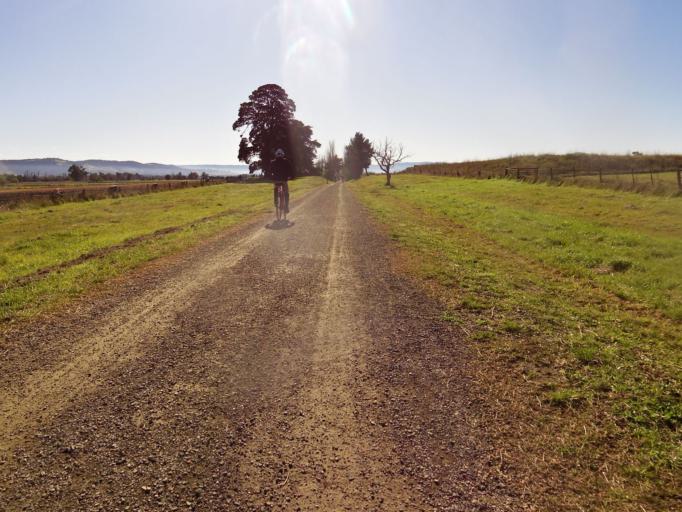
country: AU
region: Victoria
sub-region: Yarra Ranges
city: Lilydale
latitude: -37.7132
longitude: 145.3677
